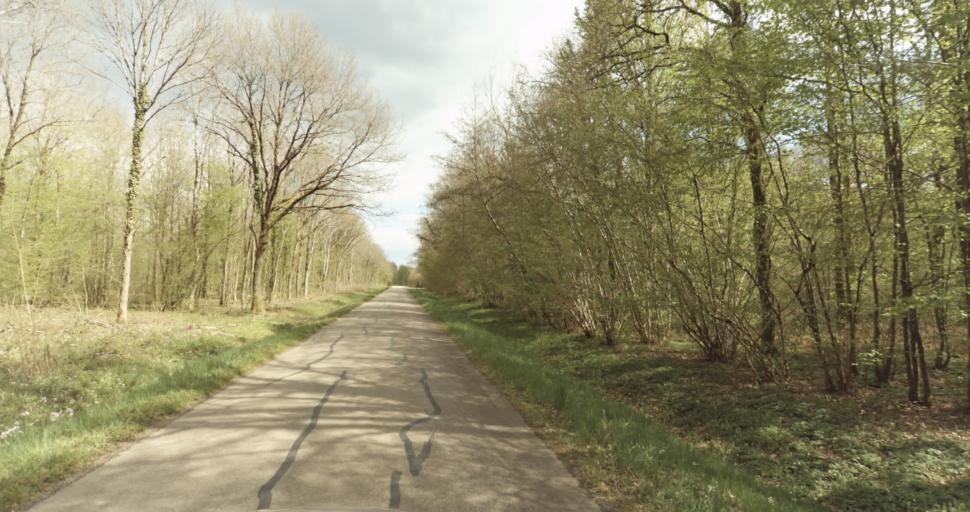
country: FR
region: Bourgogne
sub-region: Departement de la Cote-d'Or
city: Auxonne
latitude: 47.1822
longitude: 5.4522
